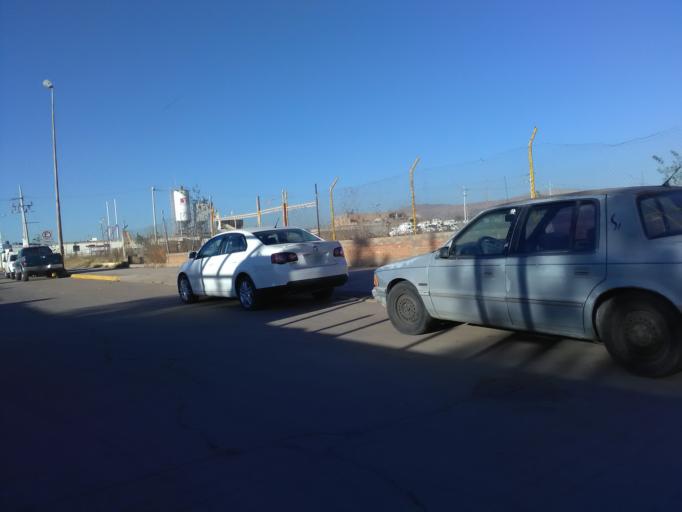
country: MX
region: Durango
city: Victoria de Durango
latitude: 24.0516
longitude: -104.6462
